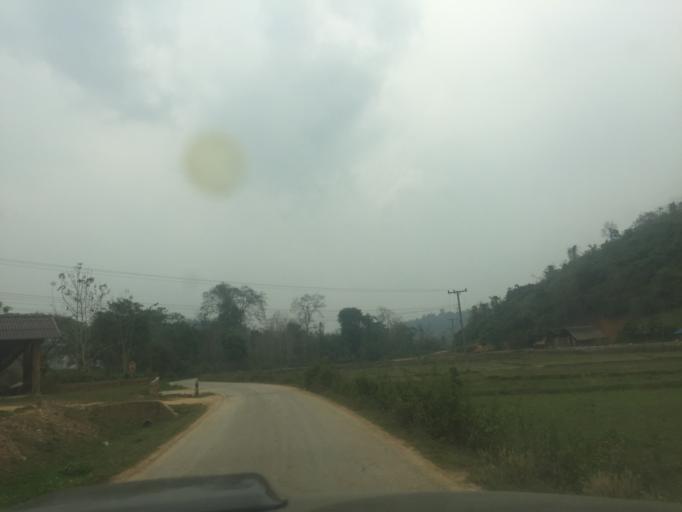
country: LA
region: Vientiane
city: Muang Sanakham
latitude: 18.3999
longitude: 101.5172
